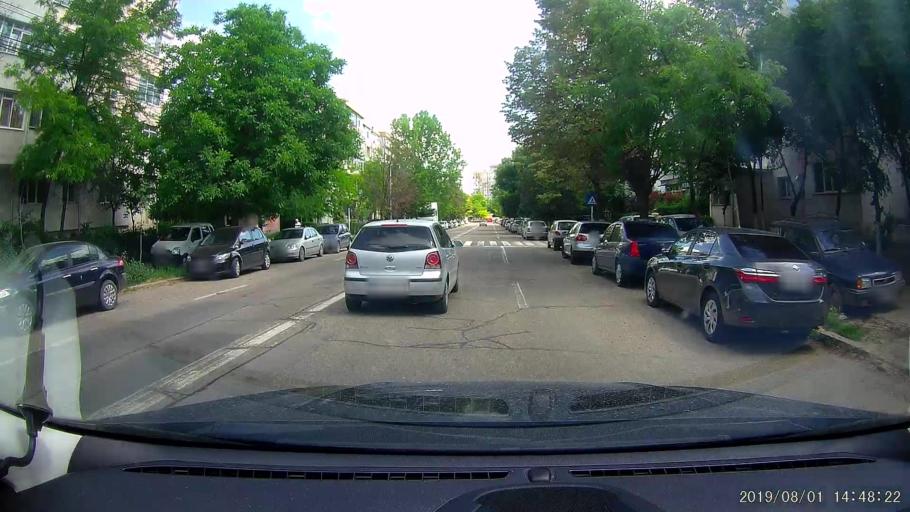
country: RO
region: Galati
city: Galati
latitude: 45.4111
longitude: 28.0085
